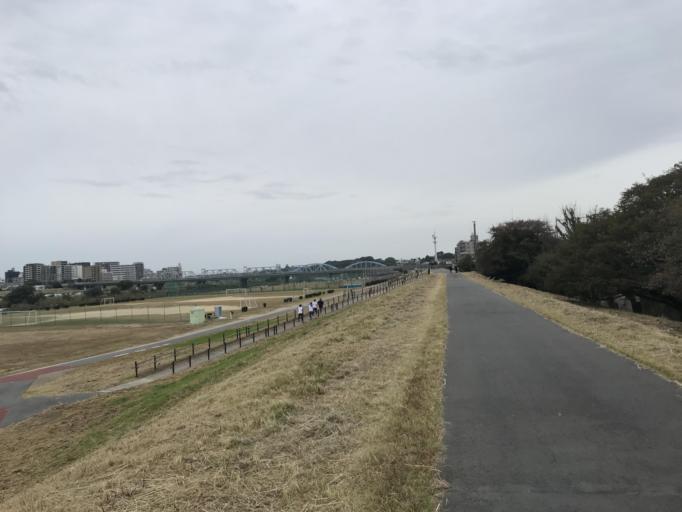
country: JP
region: Kanagawa
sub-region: Kawasaki-shi
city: Kawasaki
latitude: 35.5765
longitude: 139.6745
